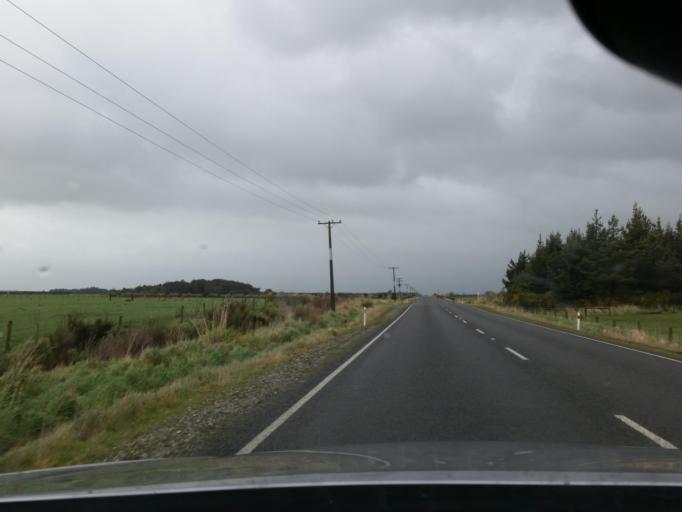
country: NZ
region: Southland
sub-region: Invercargill City
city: Invercargill
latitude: -46.4508
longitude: 168.4814
